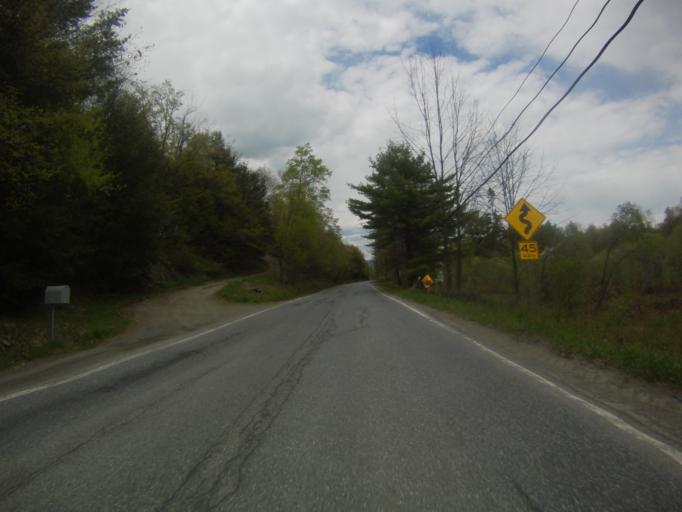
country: US
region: New York
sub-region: Essex County
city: Port Henry
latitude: 43.9900
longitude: -73.4912
